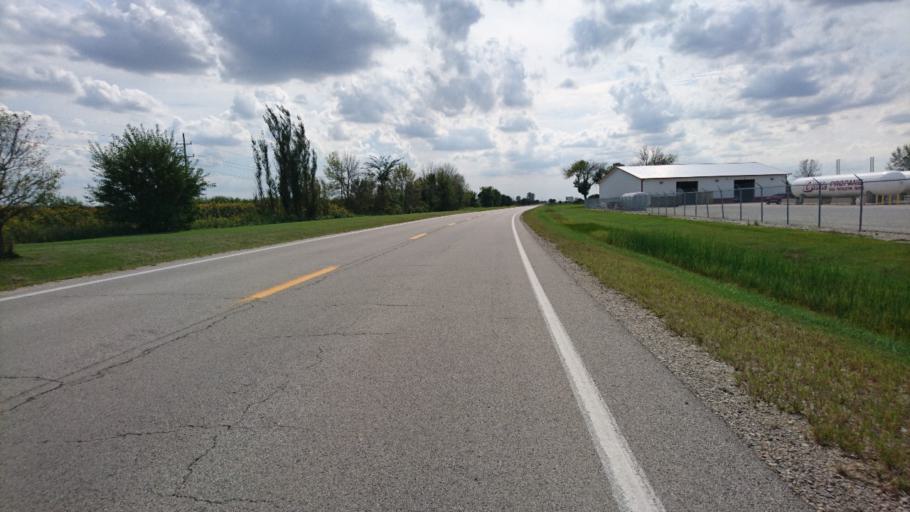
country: US
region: Illinois
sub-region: Grundy County
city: Gardner
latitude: 41.1770
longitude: -88.3225
